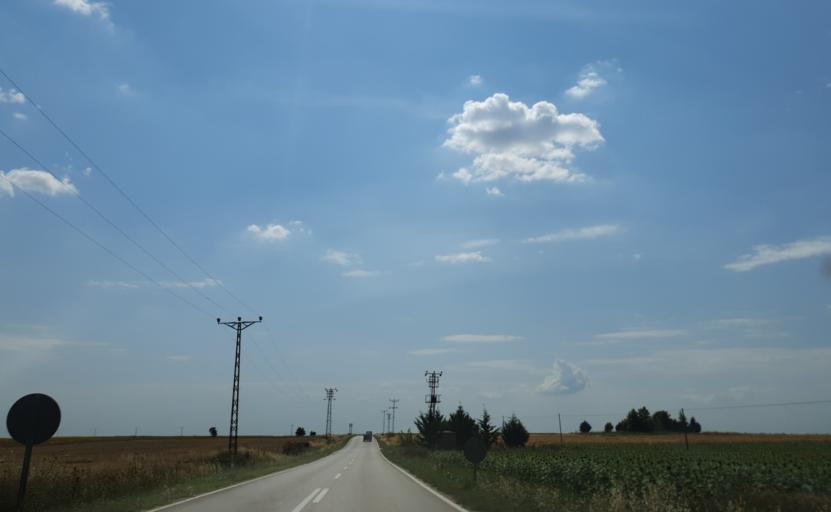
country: TR
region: Tekirdag
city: Beyazkoy
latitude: 41.4474
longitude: 27.6162
